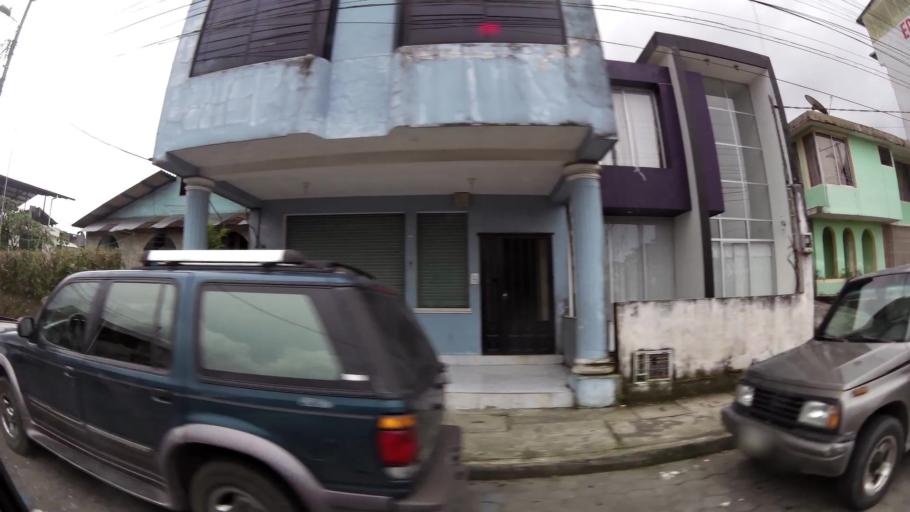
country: EC
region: Pastaza
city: Puyo
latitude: -1.4888
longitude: -77.9938
